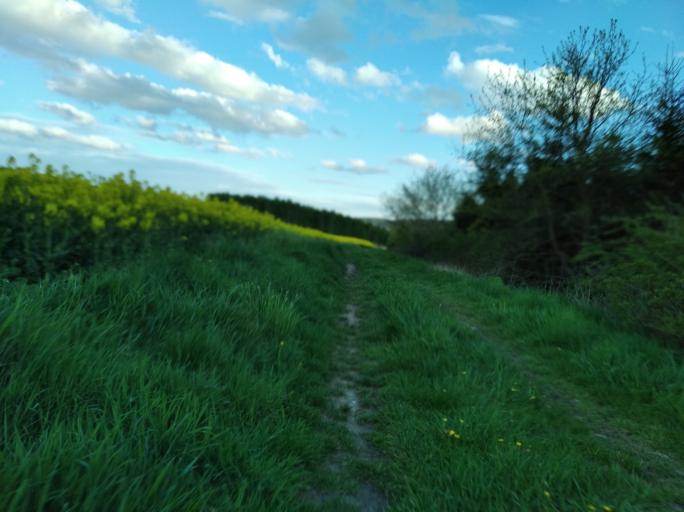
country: PL
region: Subcarpathian Voivodeship
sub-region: Powiat strzyzowski
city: Wysoka Strzyzowska
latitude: 49.8585
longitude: 21.7587
